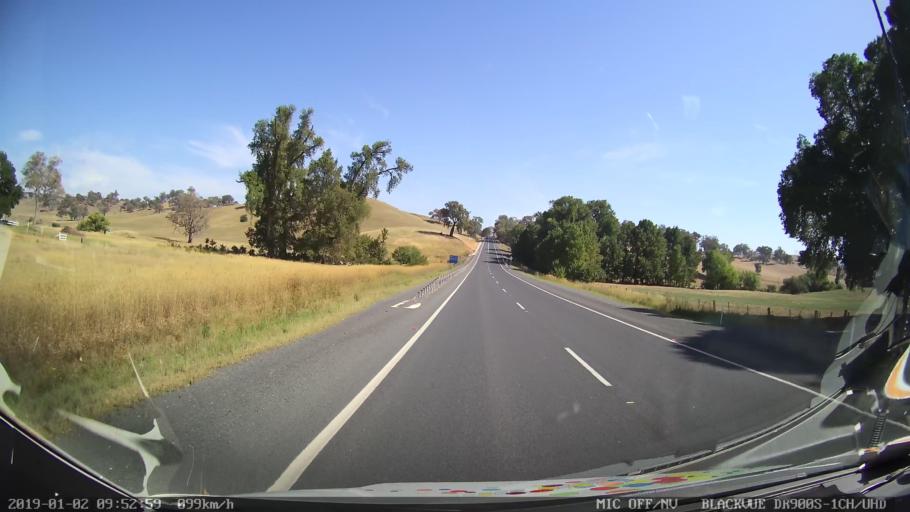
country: AU
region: New South Wales
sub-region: Tumut Shire
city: Tumut
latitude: -35.2537
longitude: 148.2038
